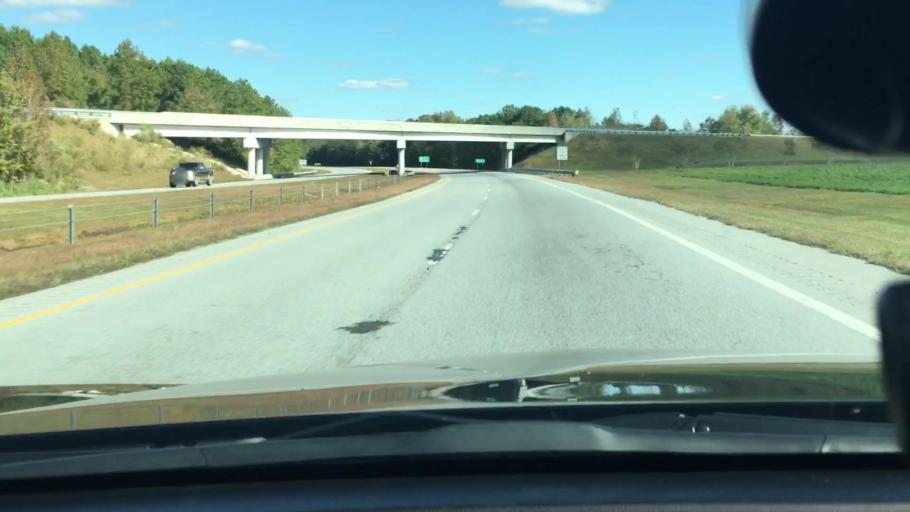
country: US
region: North Carolina
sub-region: Pitt County
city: Farmville
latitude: 35.6143
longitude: -77.6618
